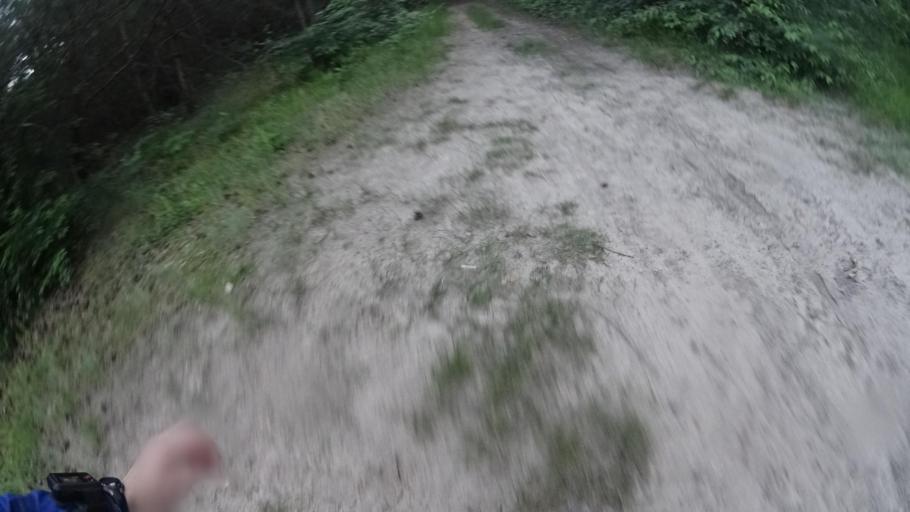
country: PL
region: Masovian Voivodeship
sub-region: Powiat warszawski zachodni
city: Truskaw
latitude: 52.2761
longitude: 20.7701
